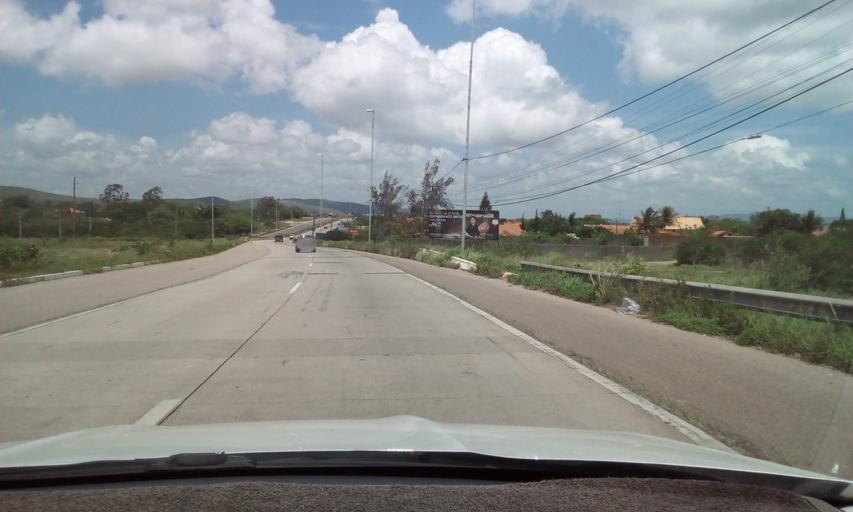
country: BR
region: Pernambuco
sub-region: Gravata
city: Gravata
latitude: -8.2033
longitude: -35.5981
